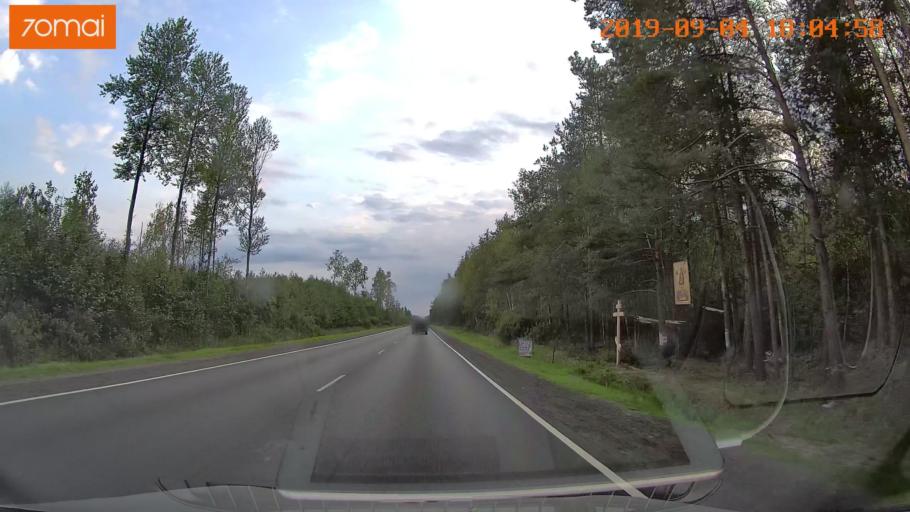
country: RU
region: Moskovskaya
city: Il'inskiy Pogost
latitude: 55.4464
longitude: 38.8323
